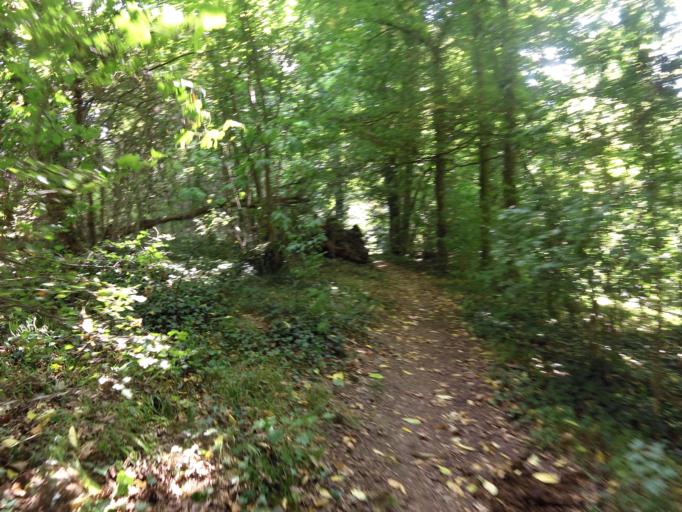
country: DE
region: Bavaria
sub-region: Regierungsbezirk Unterfranken
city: Reichenberg
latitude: 49.7389
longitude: 9.9513
